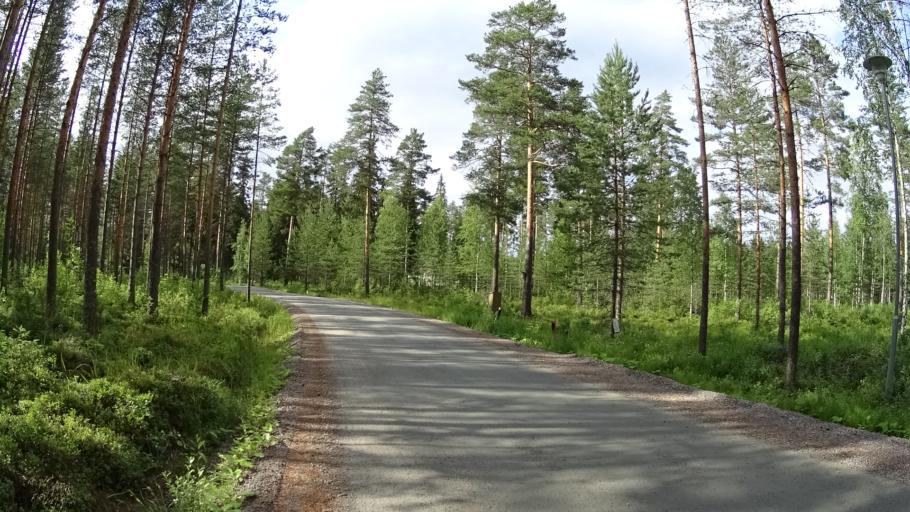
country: FI
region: Southern Ostrobothnia
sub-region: Kuusiokunnat
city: AEhtaeri
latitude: 62.5266
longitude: 24.2002
